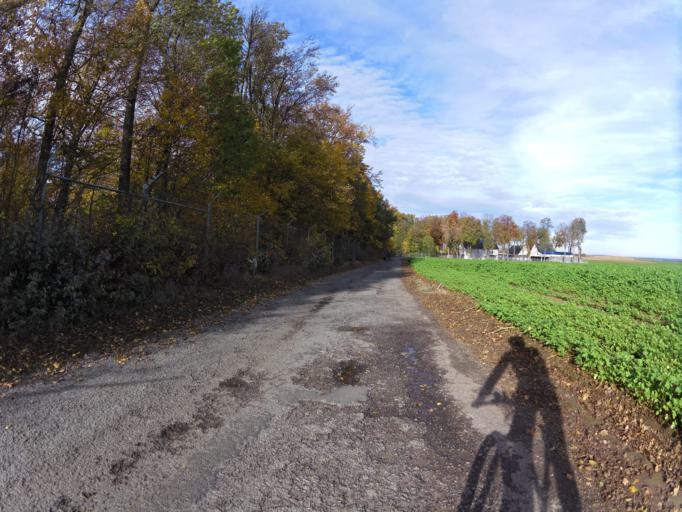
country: DE
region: Bavaria
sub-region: Regierungsbezirk Unterfranken
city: Gaukonigshofen
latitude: 49.6566
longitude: 9.9833
